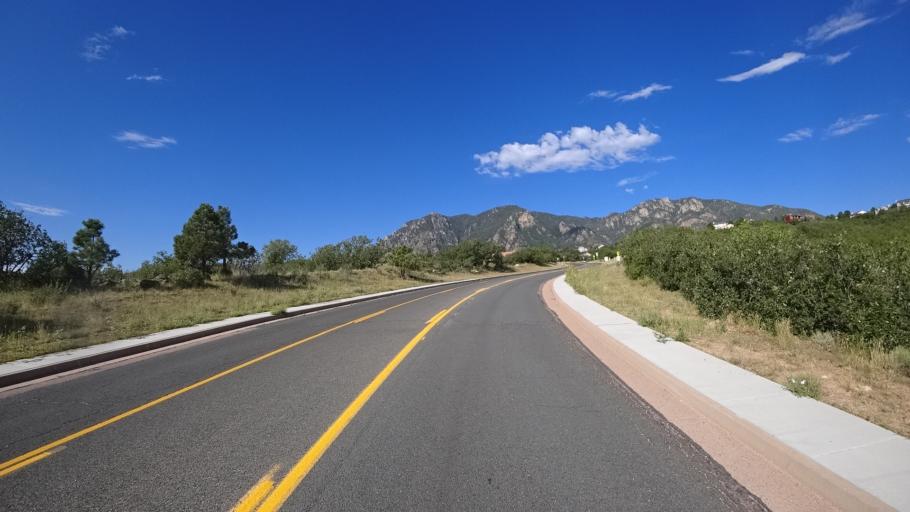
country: US
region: Colorado
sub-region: El Paso County
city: Fort Carson
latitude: 38.7610
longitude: -104.8212
